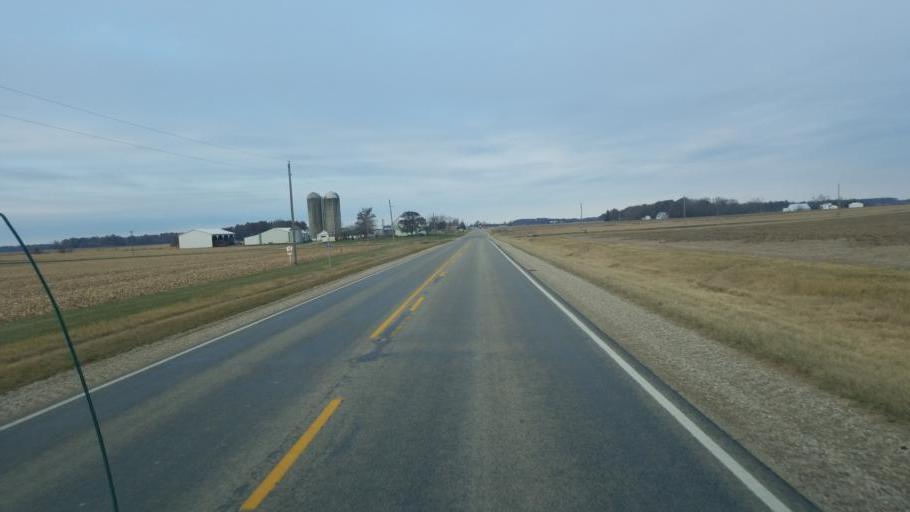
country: US
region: Indiana
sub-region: Adams County
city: Geneva
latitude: 40.5425
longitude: -84.8459
